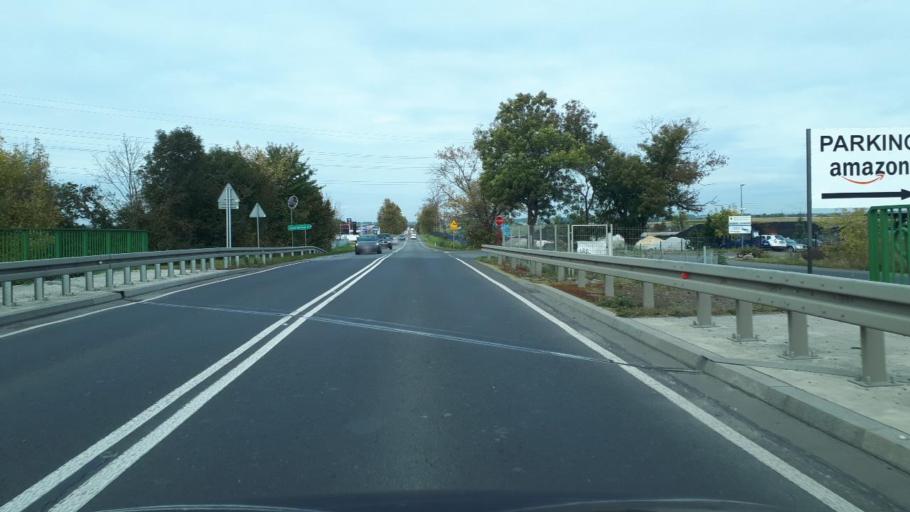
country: PL
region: Silesian Voivodeship
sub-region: Powiat gliwicki
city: Pyskowice
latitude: 50.3738
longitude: 18.6347
